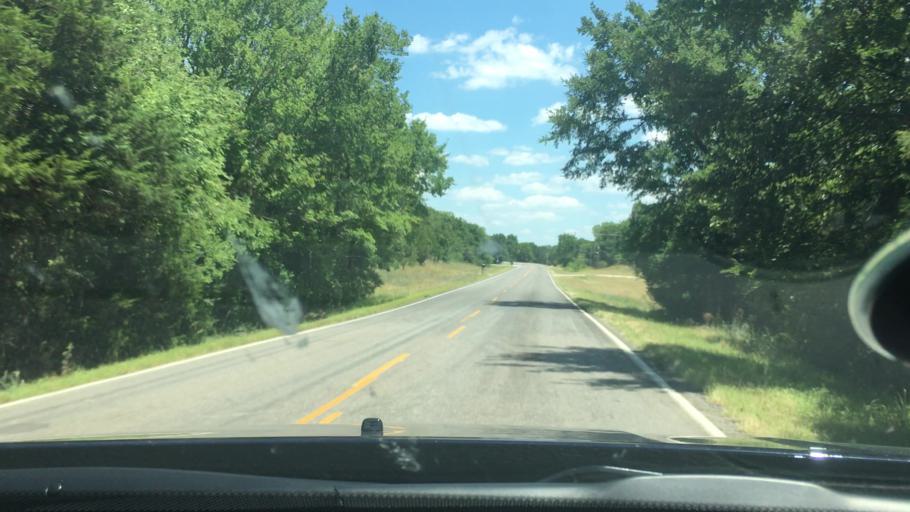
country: US
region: Oklahoma
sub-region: Carter County
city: Dickson
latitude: 34.1996
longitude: -96.9808
